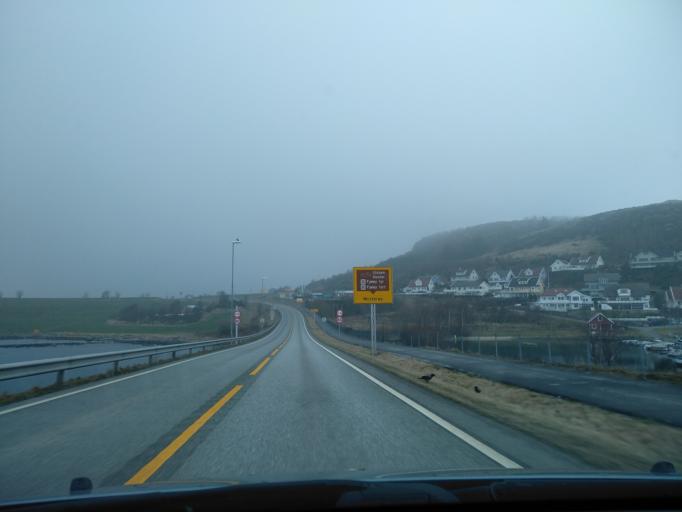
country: NO
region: Rogaland
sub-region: Rennesoy
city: Vikevag
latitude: 59.0609
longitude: 5.6772
